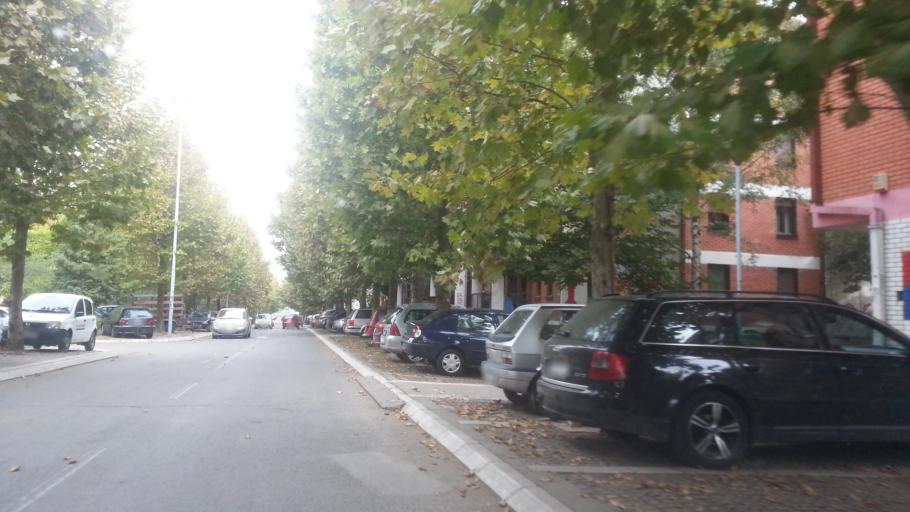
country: RS
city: Novi Banovci
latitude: 44.9661
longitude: 20.2805
